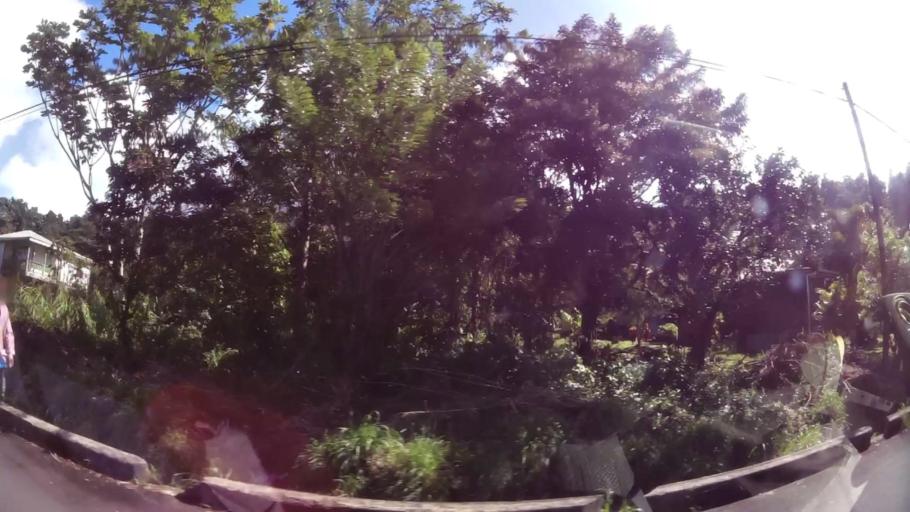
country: DM
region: Saint Paul
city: Pont Casse
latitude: 15.3645
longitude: -61.3549
